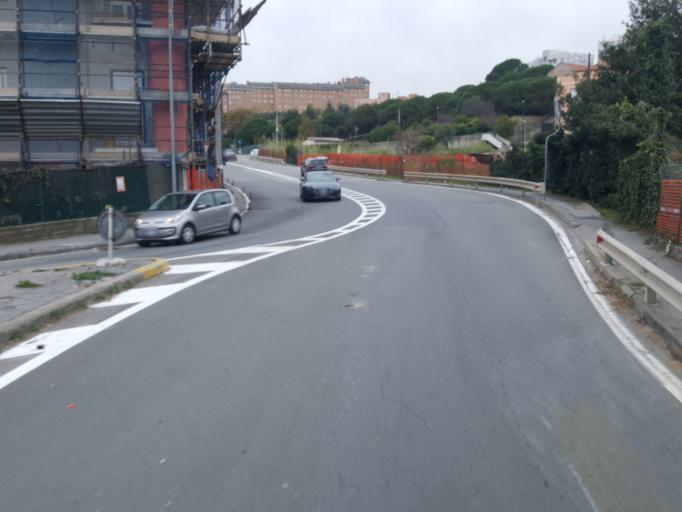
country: IT
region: Liguria
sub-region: Provincia di Savona
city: Valleggia
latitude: 44.2939
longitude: 8.4526
